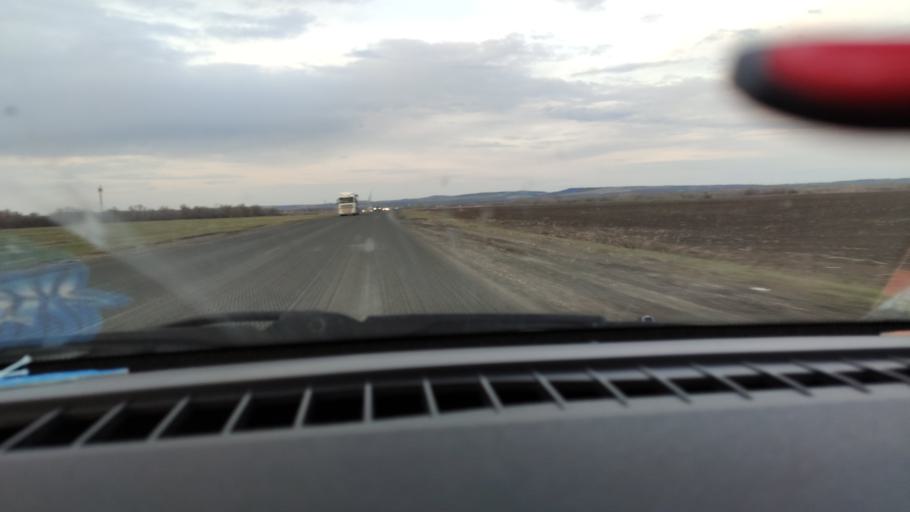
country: RU
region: Saratov
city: Yelshanka
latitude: 51.8140
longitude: 46.2073
